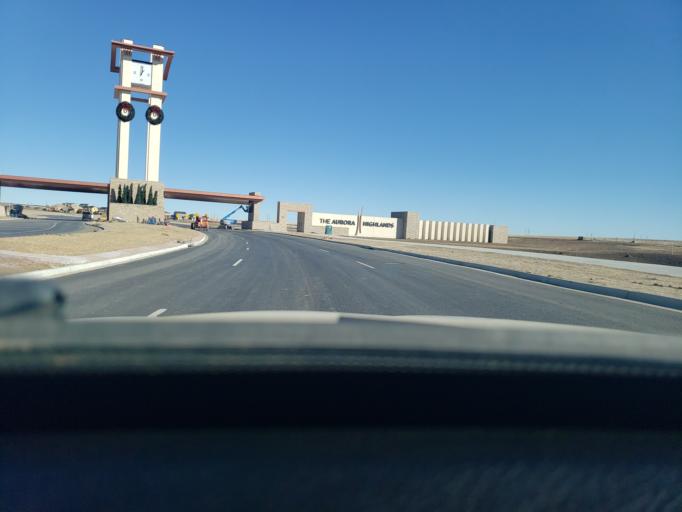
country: US
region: Colorado
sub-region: Adams County
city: Aurora
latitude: 39.7692
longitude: -104.7109
